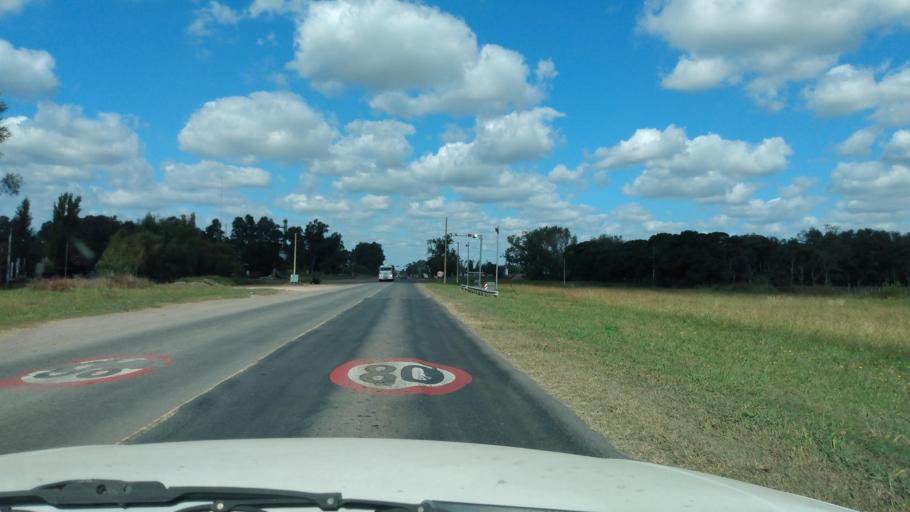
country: AR
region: Buenos Aires
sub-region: Partido de Navarro
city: Navarro
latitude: -34.9929
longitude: -59.3149
